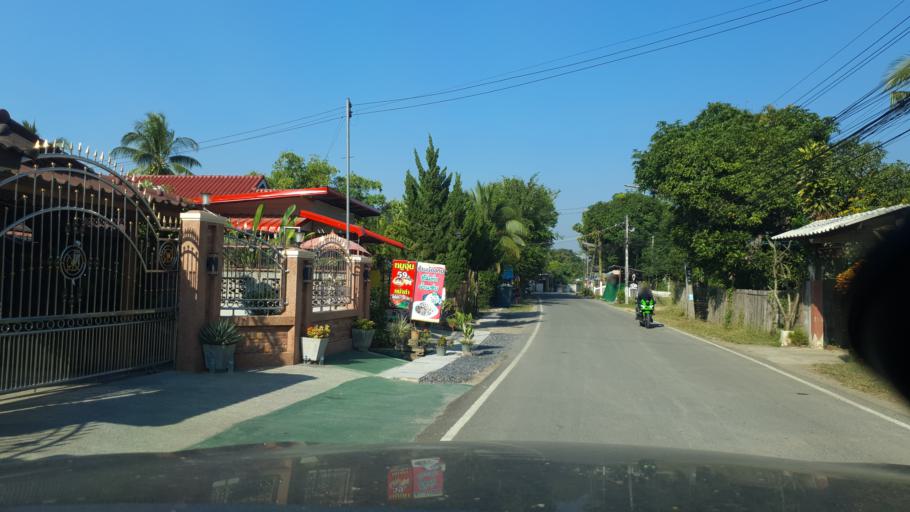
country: TH
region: Chiang Mai
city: San Kamphaeng
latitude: 18.7521
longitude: 99.1646
